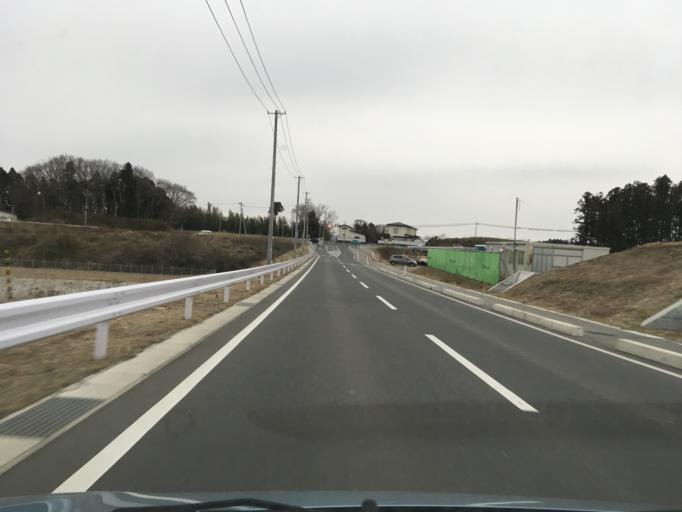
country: JP
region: Miyagi
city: Wakuya
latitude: 38.6941
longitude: 141.1710
